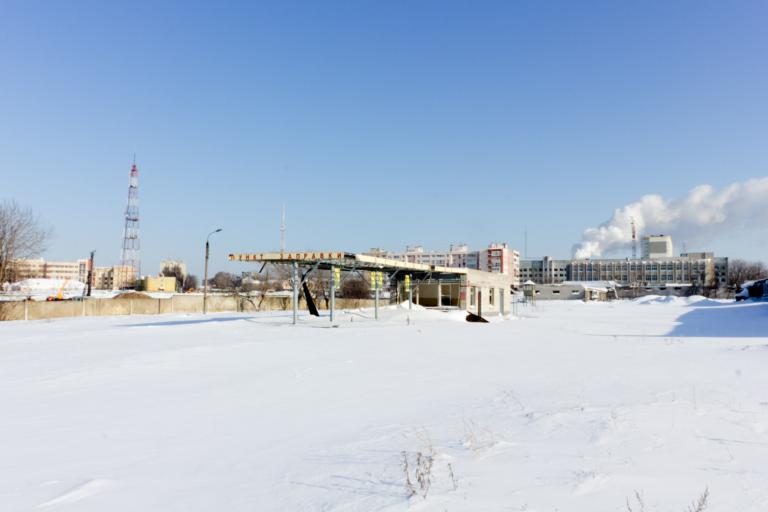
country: RU
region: Nizjnij Novgorod
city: Nizhniy Novgorod
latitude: 56.3030
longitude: 43.9730
